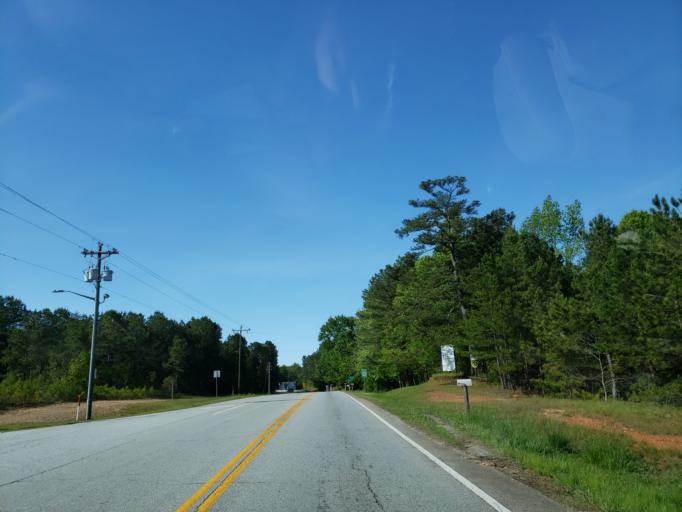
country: US
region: Georgia
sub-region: Haralson County
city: Tallapoosa
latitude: 33.6887
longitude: -85.2617
